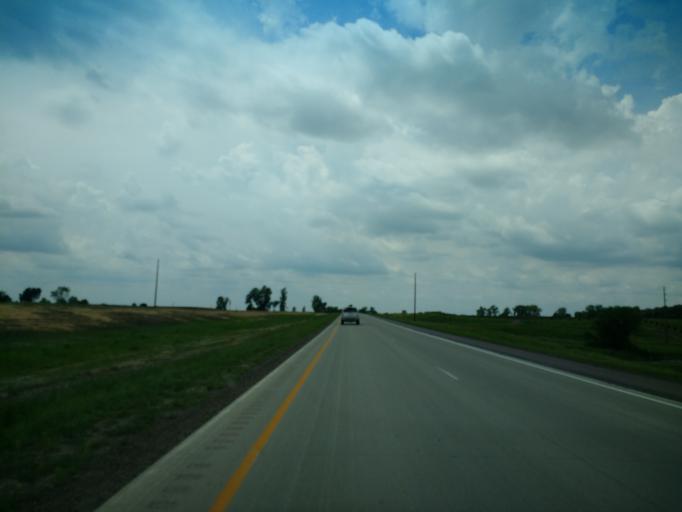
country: US
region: Minnesota
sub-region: Cottonwood County
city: Windom
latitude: 43.9049
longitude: -95.0596
